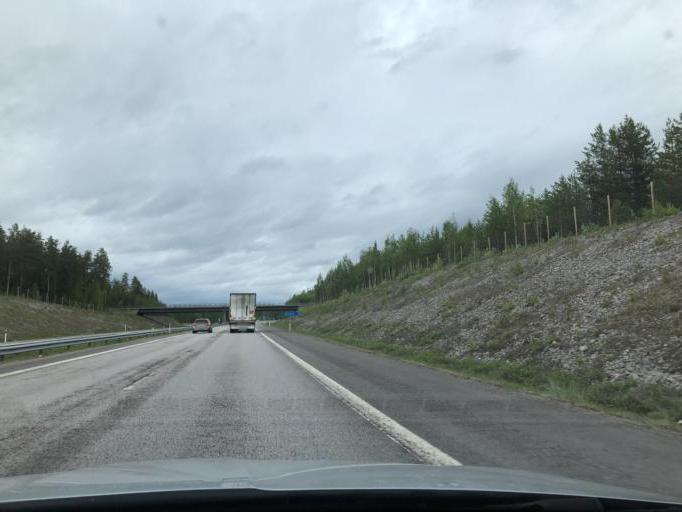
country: SE
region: Norrbotten
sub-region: Pitea Kommun
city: Norrfjarden
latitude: 65.3706
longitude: 21.4295
